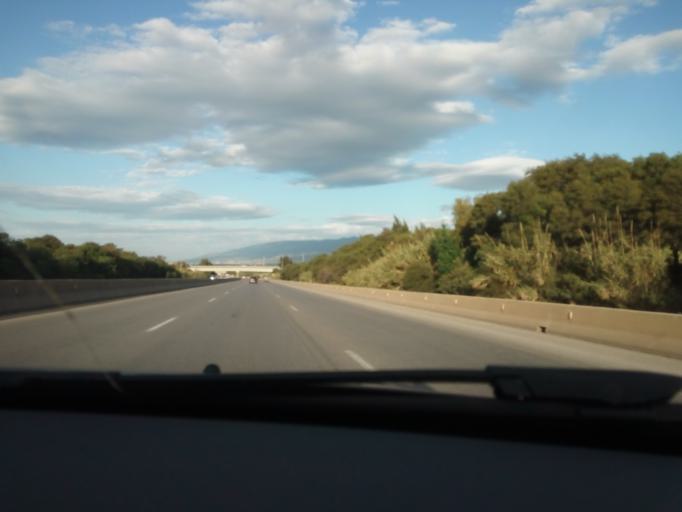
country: DZ
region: Tipaza
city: El Affroun
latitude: 36.4461
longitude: 2.6359
